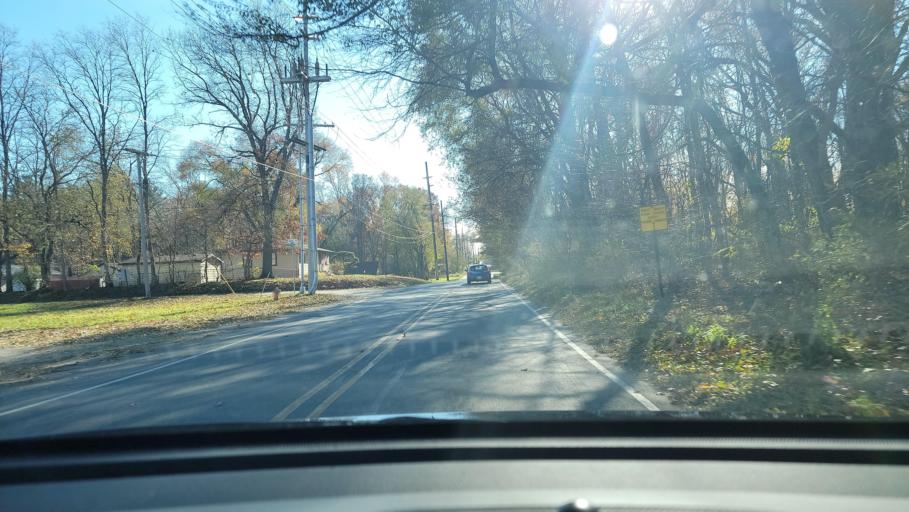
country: US
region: Indiana
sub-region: Porter County
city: Portage
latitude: 41.5967
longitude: -87.1835
